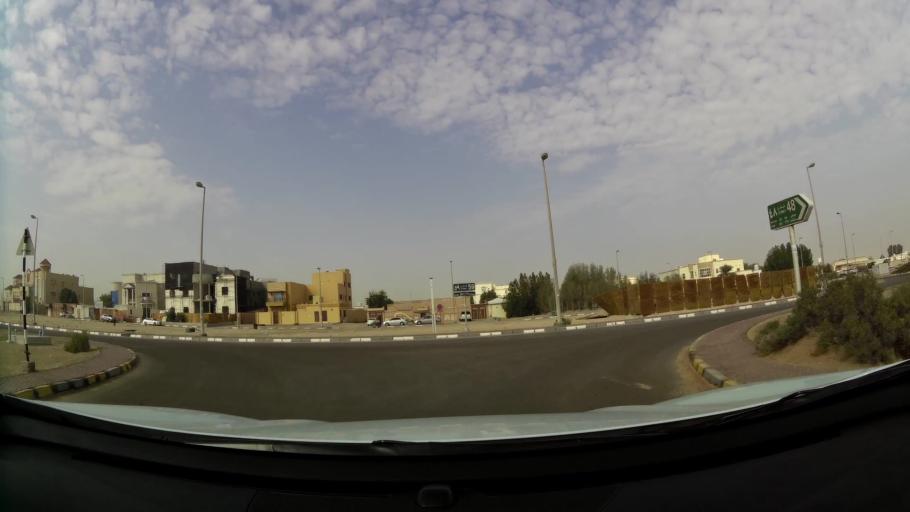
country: AE
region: Abu Dhabi
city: Abu Dhabi
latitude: 24.2597
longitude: 54.7106
